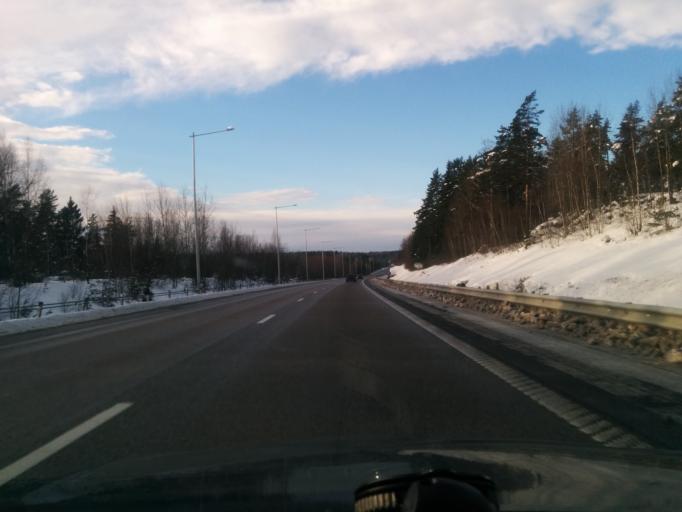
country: SE
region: Stockholm
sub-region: Upplands-Bro Kommun
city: Bro
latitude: 59.5117
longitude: 17.6890
